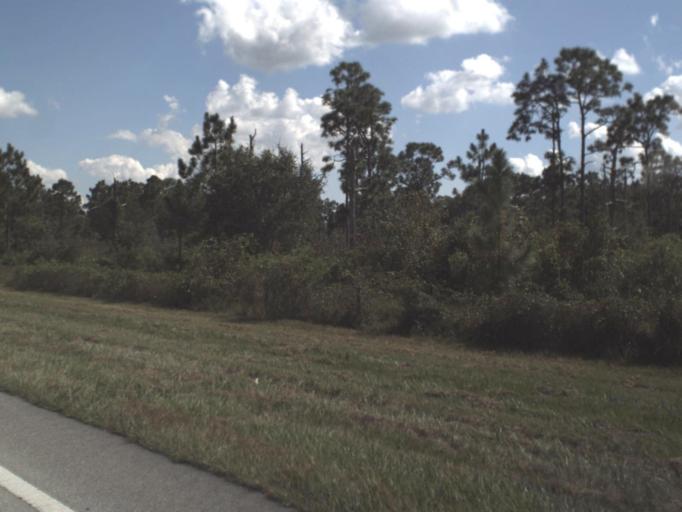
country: US
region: Florida
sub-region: Okeechobee County
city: Okeechobee
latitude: 27.3888
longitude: -81.0265
